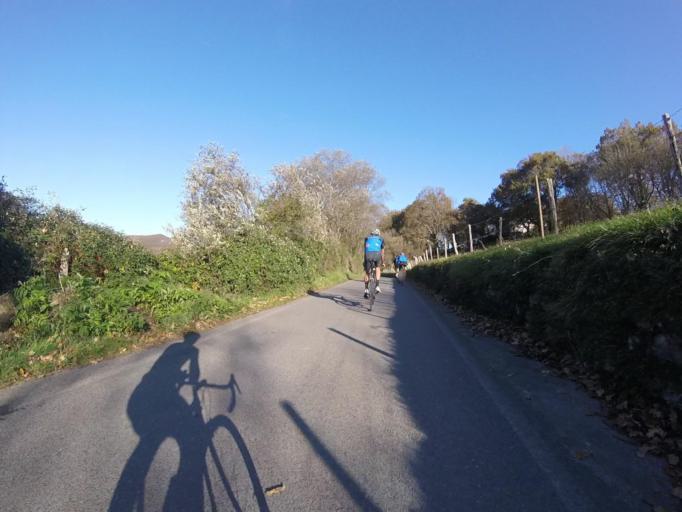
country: ES
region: Navarre
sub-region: Provincia de Navarra
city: Igantzi
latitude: 43.2273
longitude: -1.7036
